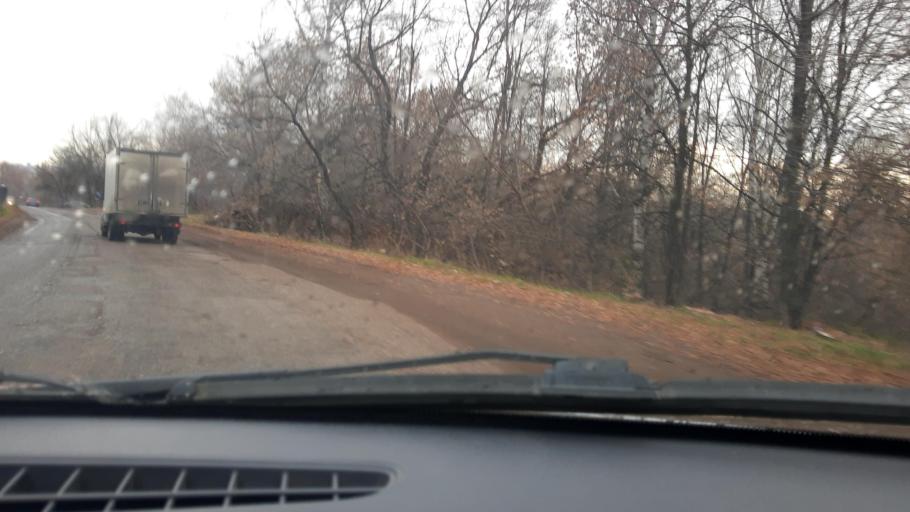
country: RU
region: Bashkortostan
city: Avdon
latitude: 54.7011
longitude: 55.8096
